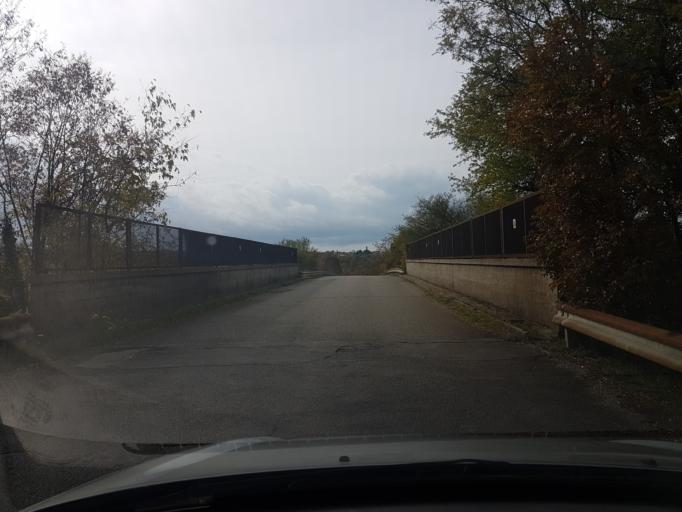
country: IT
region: Friuli Venezia Giulia
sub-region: Provincia di Trieste
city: Santa Croce
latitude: 45.7393
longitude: 13.7081
